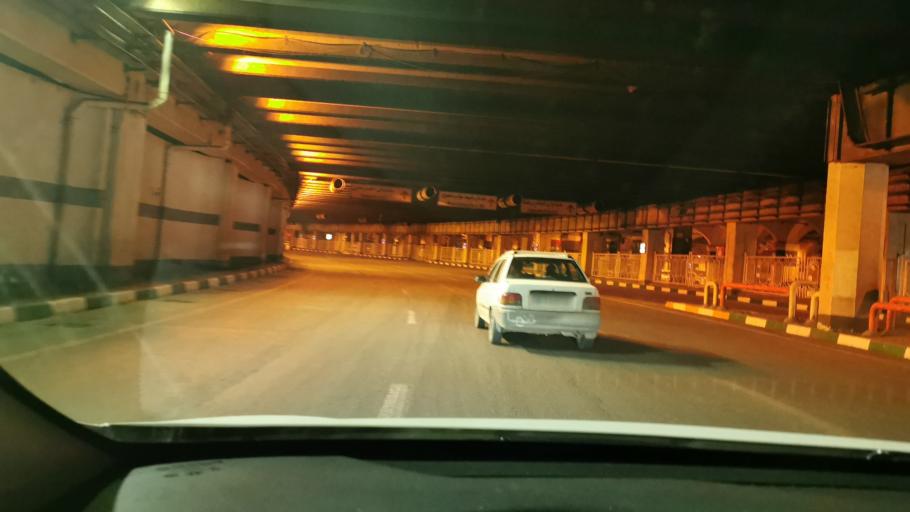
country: IR
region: Razavi Khorasan
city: Mashhad
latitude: 36.2898
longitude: 59.6152
